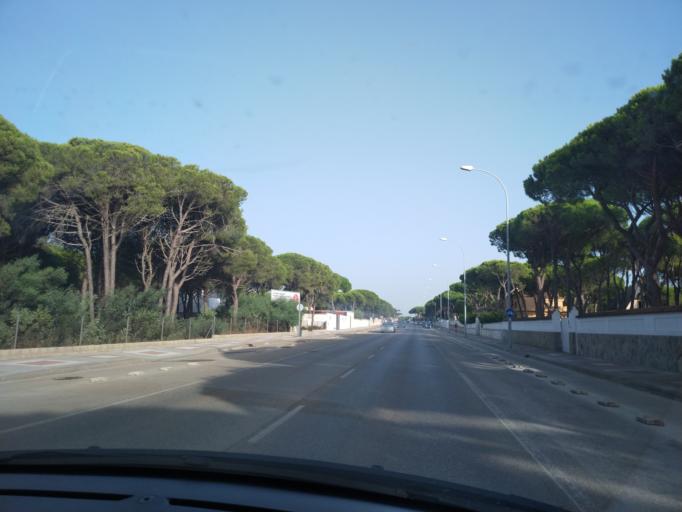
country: ES
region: Andalusia
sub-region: Provincia de Cadiz
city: Chiclana de la Frontera
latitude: 36.3795
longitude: -6.1906
